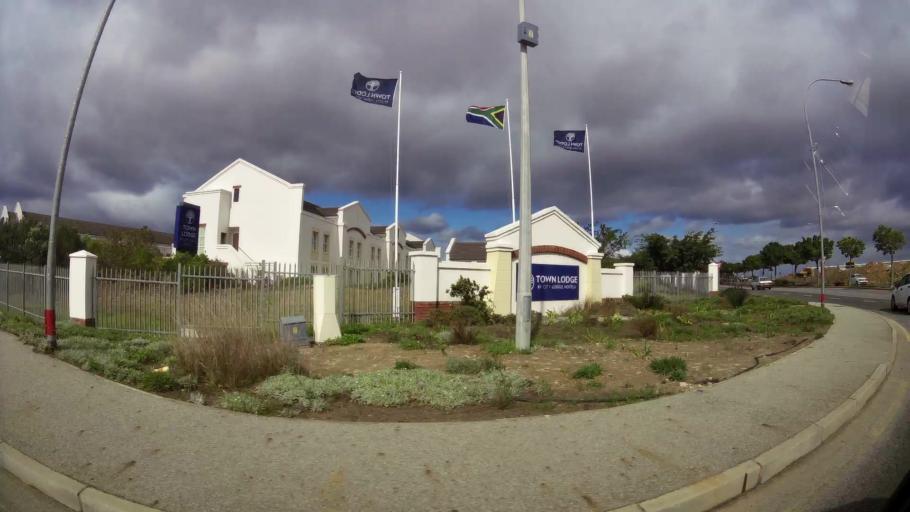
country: ZA
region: Western Cape
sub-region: Eden District Municipality
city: George
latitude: -33.9842
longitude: 22.5024
